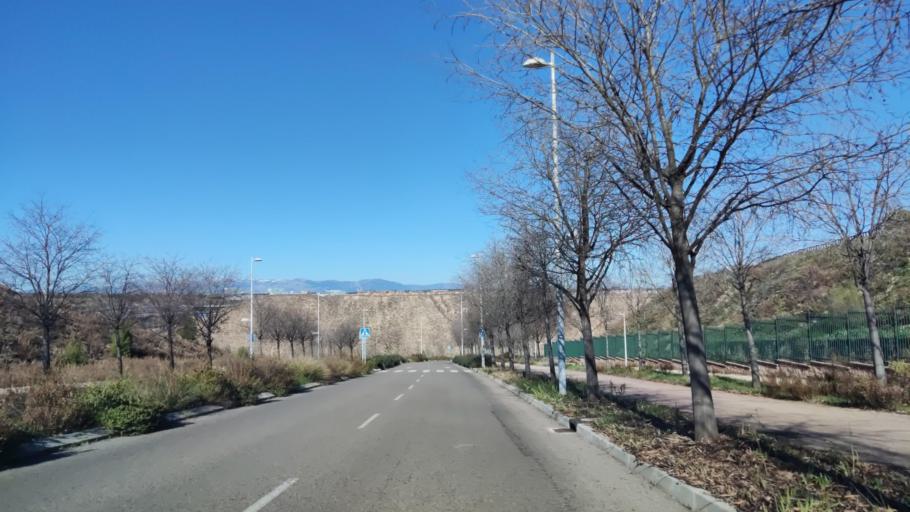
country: ES
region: Madrid
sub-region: Provincia de Madrid
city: Hortaleza
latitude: 40.4922
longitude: -3.6429
